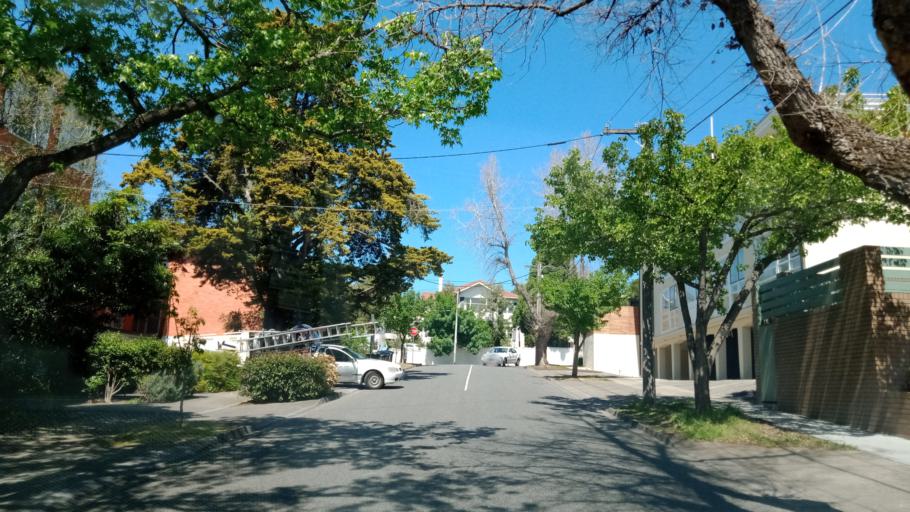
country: AU
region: Victoria
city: Toorak
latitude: -37.8427
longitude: 145.0271
